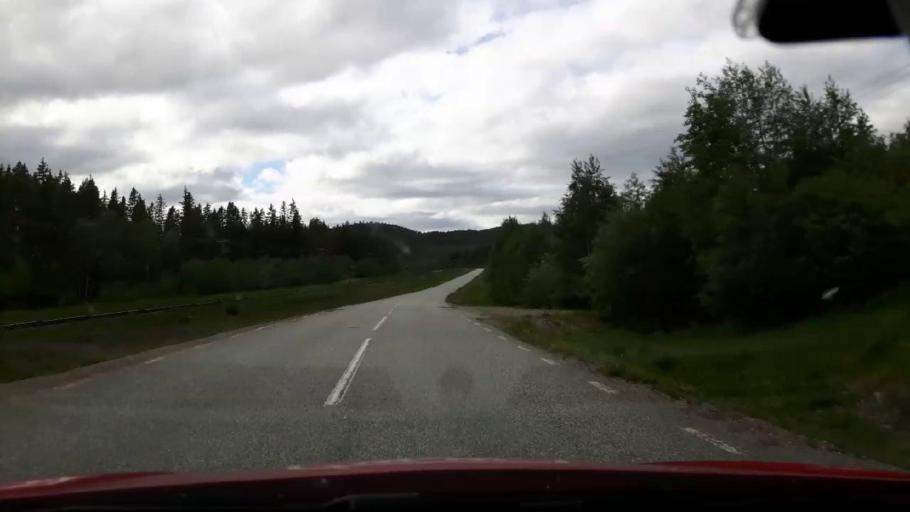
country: SE
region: Jaemtland
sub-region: Ragunda Kommun
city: Hammarstrand
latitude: 62.9649
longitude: 16.0239
